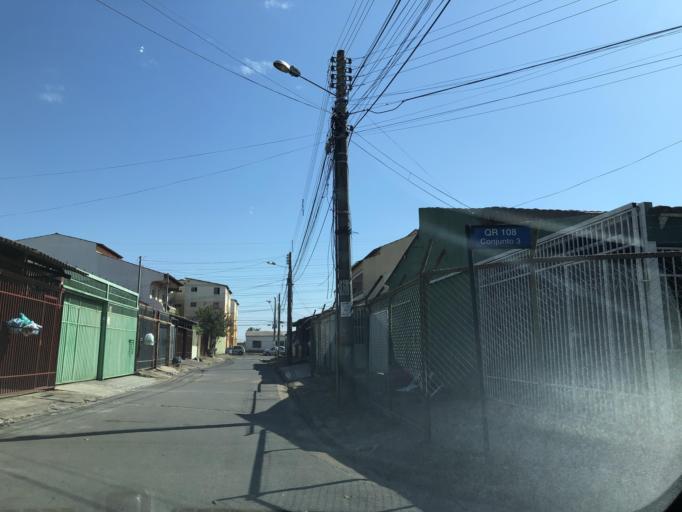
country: BR
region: Federal District
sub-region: Brasilia
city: Brasilia
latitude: -15.8720
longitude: -48.0774
